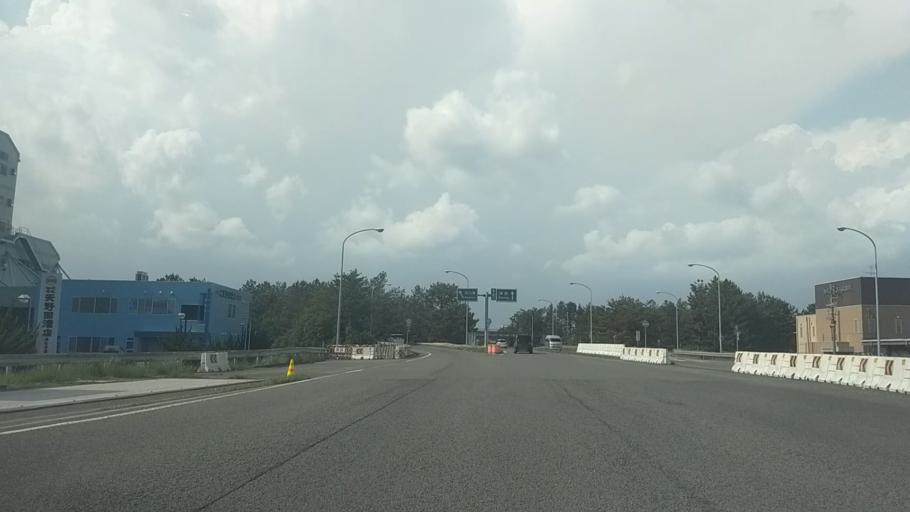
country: JP
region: Shizuoka
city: Hamakita
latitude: 34.7453
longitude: 137.7887
